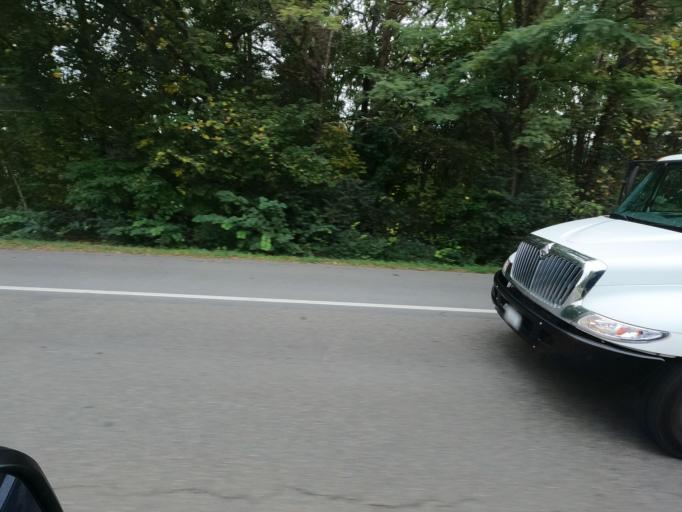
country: US
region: Tennessee
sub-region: Sullivan County
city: Kingsport
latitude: 36.5555
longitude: -82.5954
